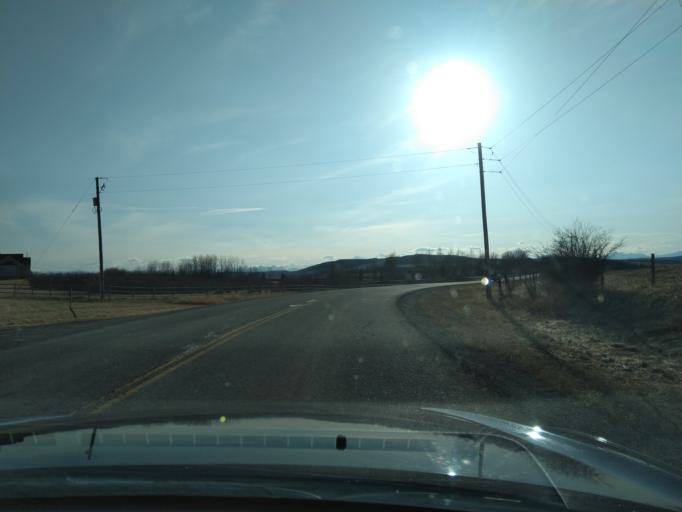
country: CA
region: Alberta
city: Cochrane
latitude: 51.1679
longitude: -114.4829
